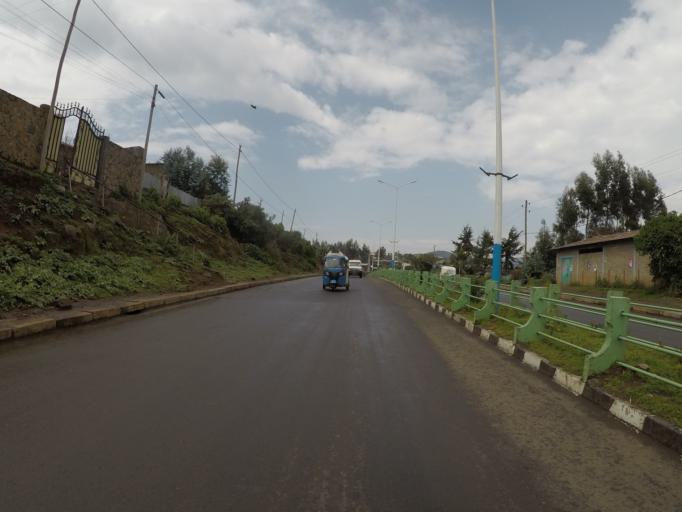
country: ET
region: Amhara
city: Debark'
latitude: 13.1500
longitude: 37.8950
